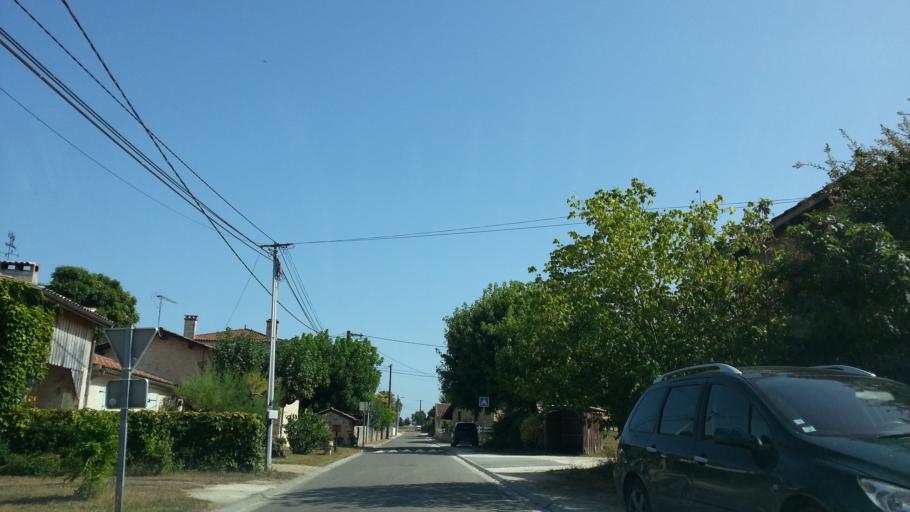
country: FR
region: Aquitaine
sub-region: Departement de la Gironde
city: Landiras
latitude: 44.5813
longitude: -0.3989
